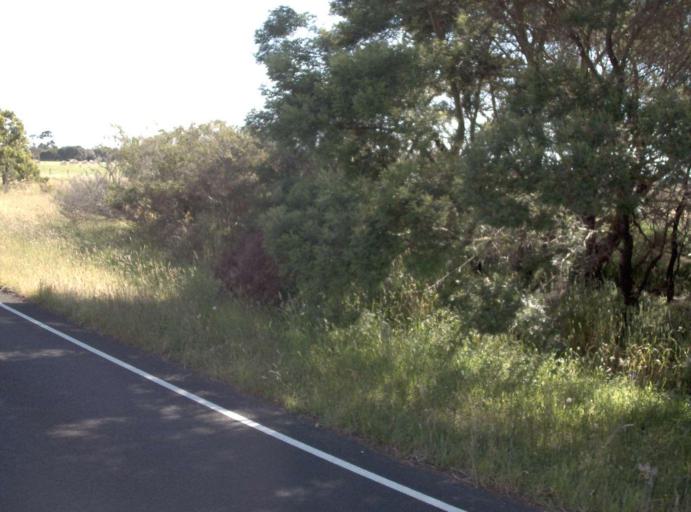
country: AU
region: Victoria
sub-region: Latrobe
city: Traralgon
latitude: -38.6314
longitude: 146.6761
